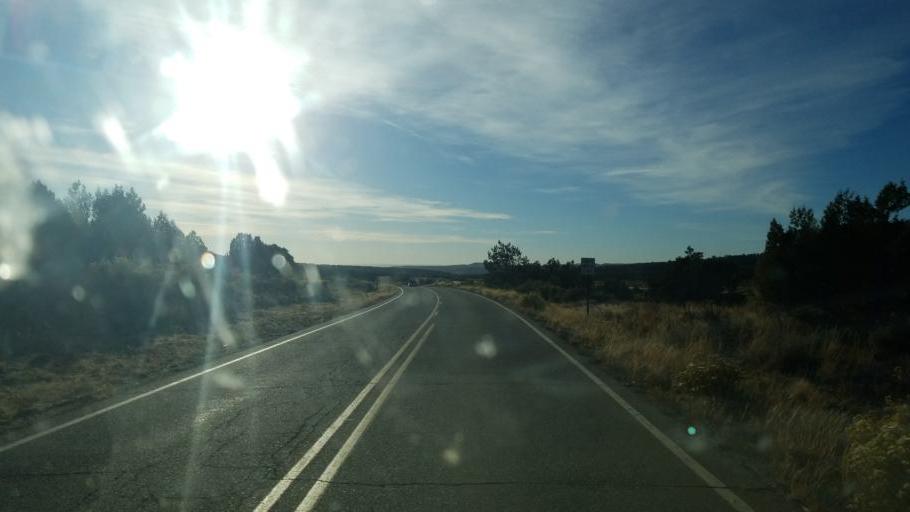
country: US
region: New Mexico
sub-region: San Juan County
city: Bloomfield
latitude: 36.7364
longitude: -107.7475
